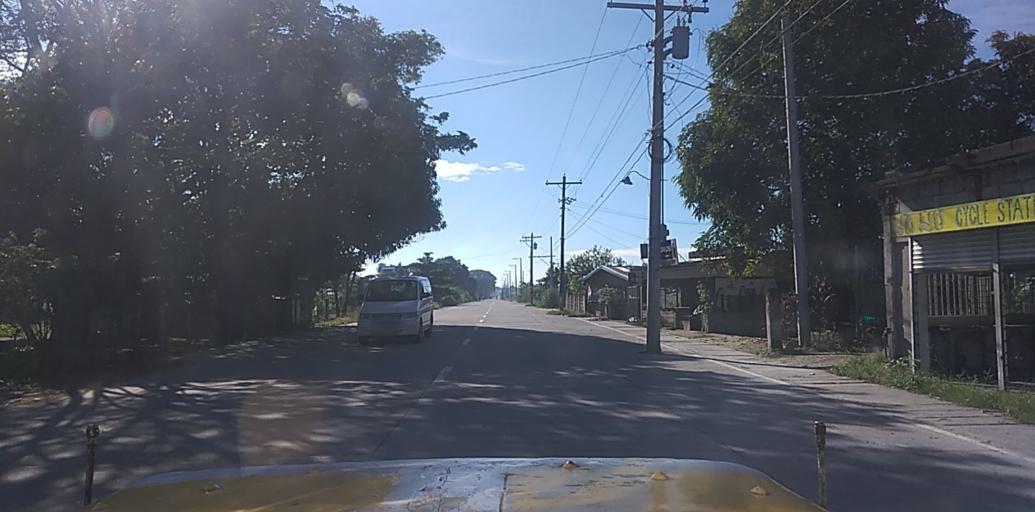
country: PH
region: Central Luzon
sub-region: Province of Pampanga
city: Anao
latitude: 15.1334
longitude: 120.6961
